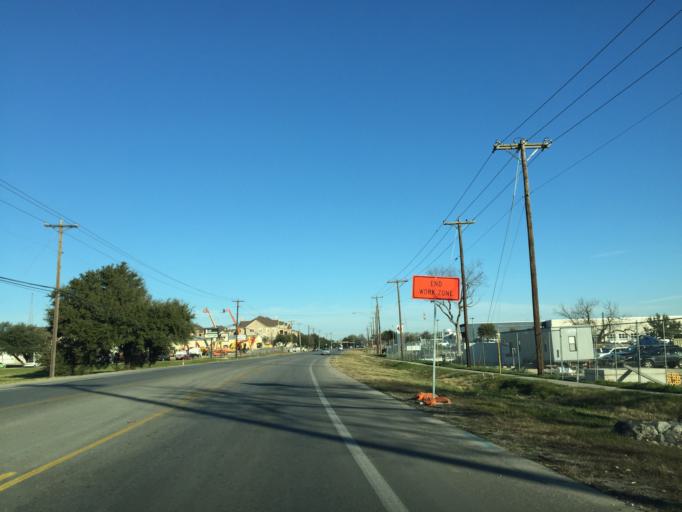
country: US
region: Texas
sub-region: Williamson County
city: Jollyville
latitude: 30.4372
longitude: -97.7714
